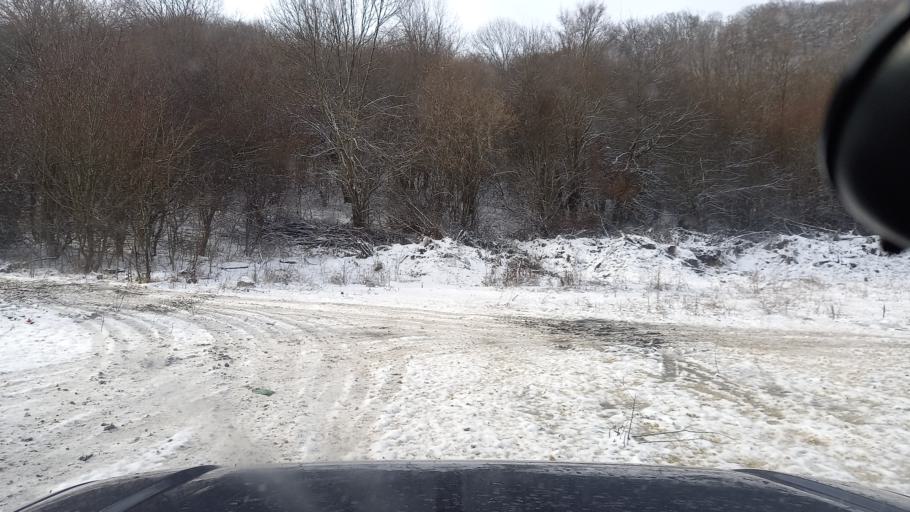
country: RU
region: Adygeya
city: Kamennomostskiy
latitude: 44.2449
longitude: 40.1972
